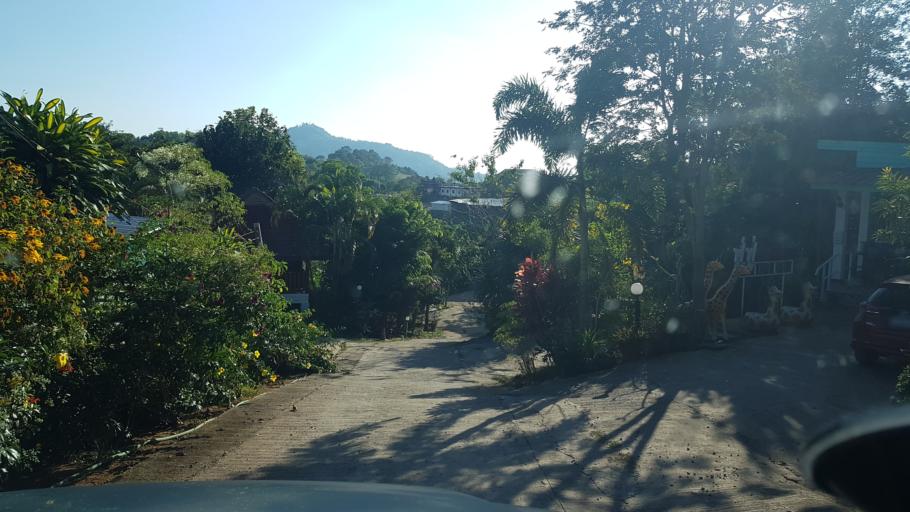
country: TH
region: Phetchabun
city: Khao Kho
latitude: 16.6464
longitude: 101.0000
